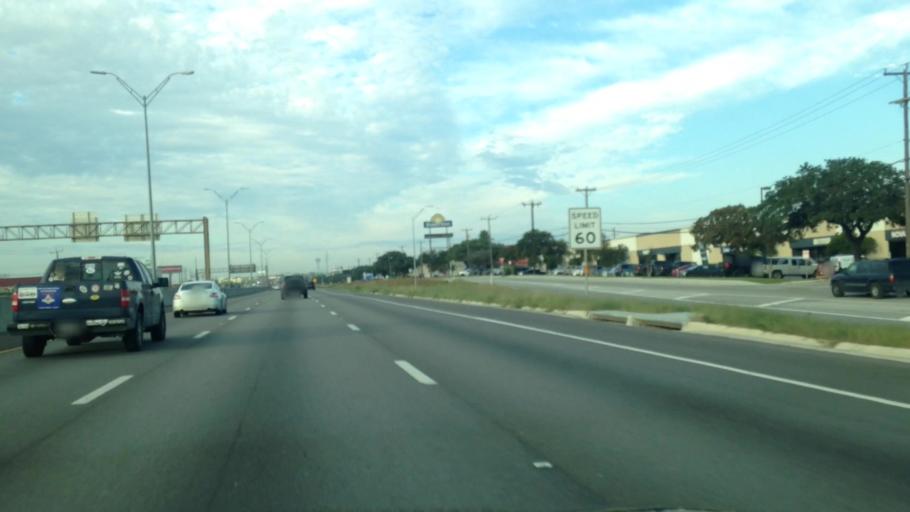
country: US
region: Texas
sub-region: Bexar County
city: Terrell Hills
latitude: 29.4472
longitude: -98.4293
